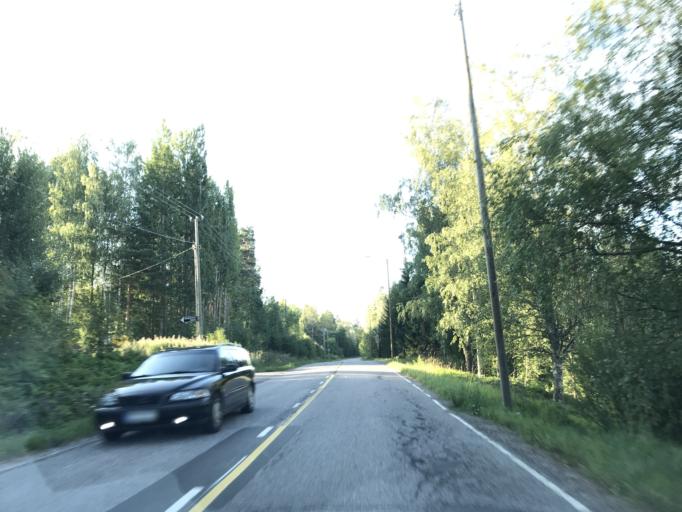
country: FI
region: Uusimaa
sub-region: Helsinki
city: Nurmijaervi
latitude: 60.3712
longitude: 24.6792
